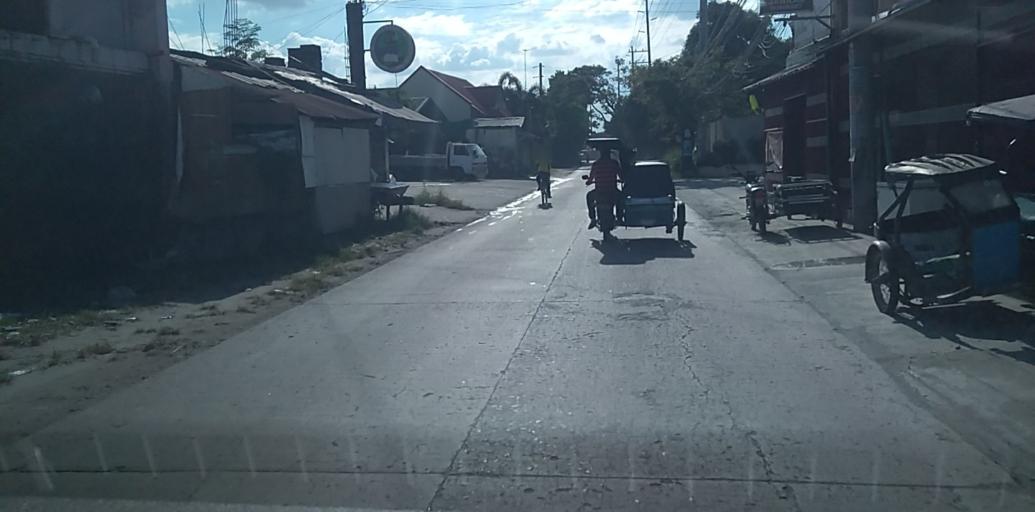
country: PH
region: Central Luzon
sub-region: Province of Pampanga
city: Acli
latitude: 15.1114
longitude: 120.6307
